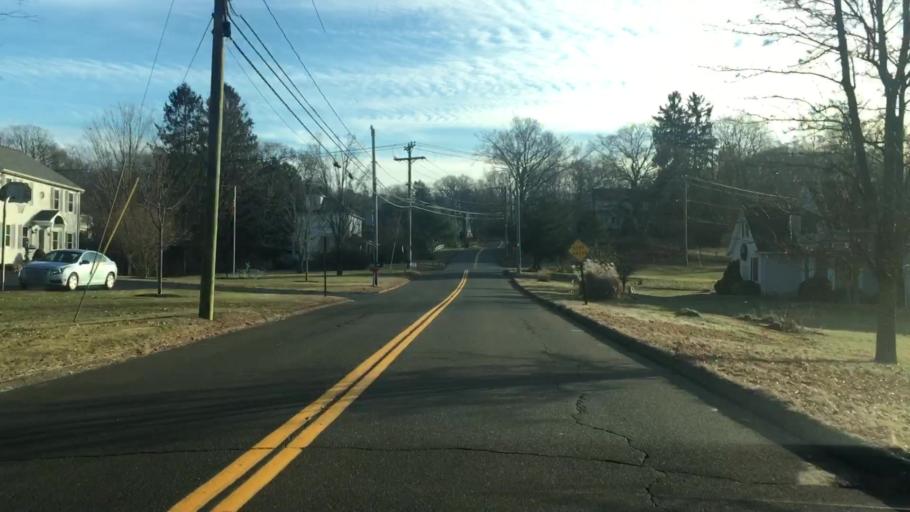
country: US
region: Connecticut
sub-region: Middlesex County
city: Middletown
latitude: 41.5216
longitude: -72.6493
